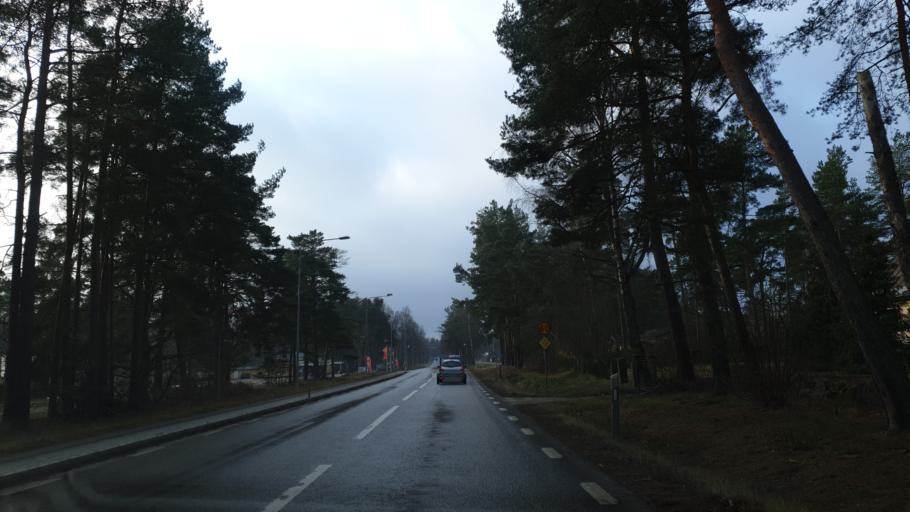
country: SE
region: Blekinge
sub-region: Karlshamns Kommun
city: Morrum
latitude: 56.1546
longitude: 14.6744
